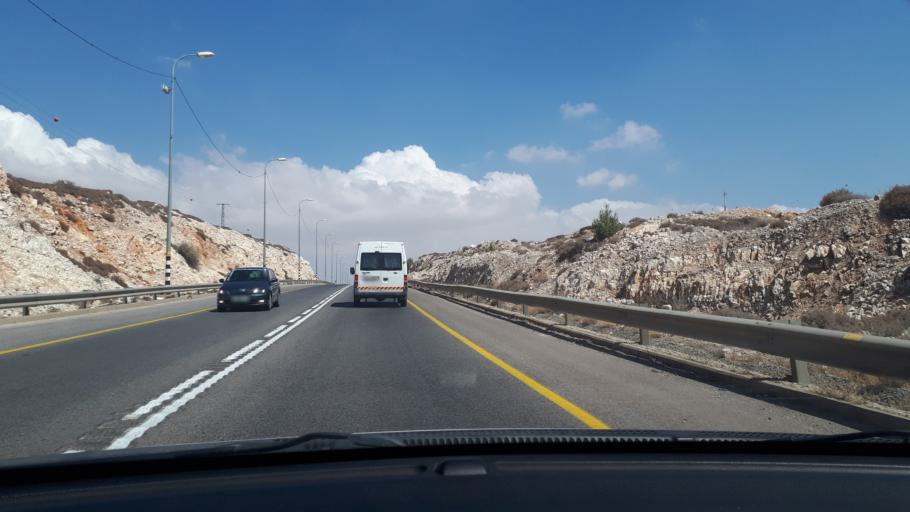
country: PS
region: West Bank
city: Burqah
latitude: 31.8957
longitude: 35.2693
